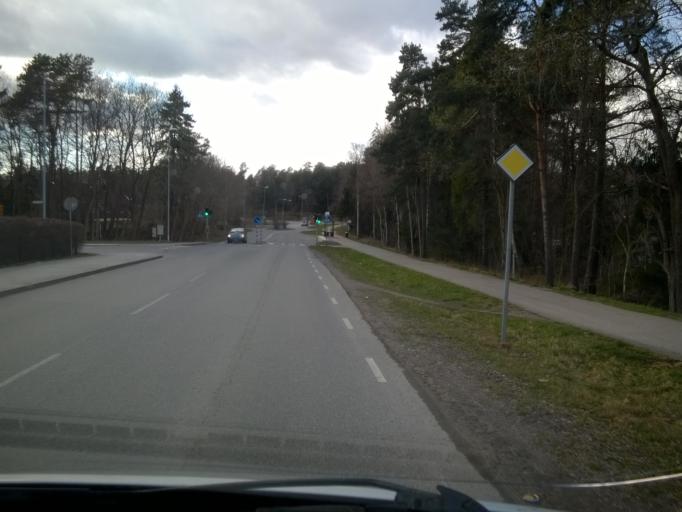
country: SE
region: Stockholm
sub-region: Jarfalla Kommun
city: Jakobsberg
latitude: 59.3852
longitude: 17.8276
